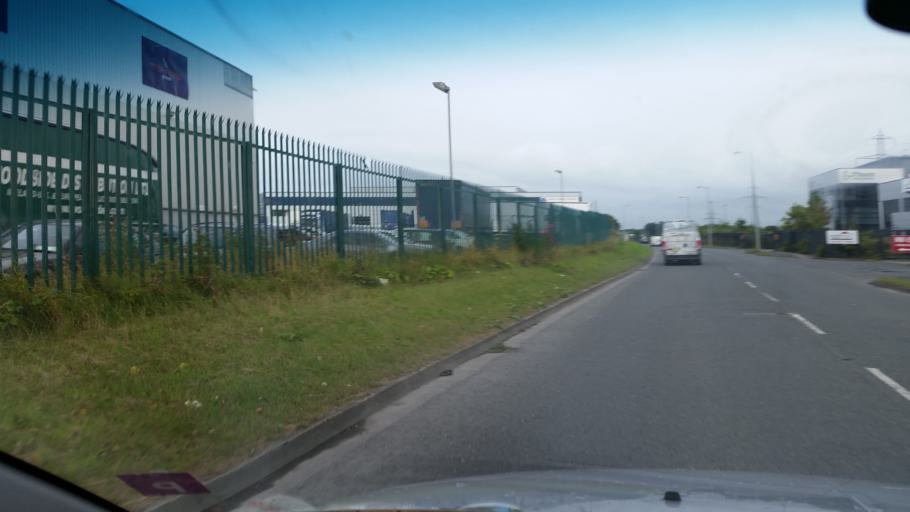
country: IE
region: Leinster
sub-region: Fingal County
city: Blanchardstown
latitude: 53.4138
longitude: -6.3519
